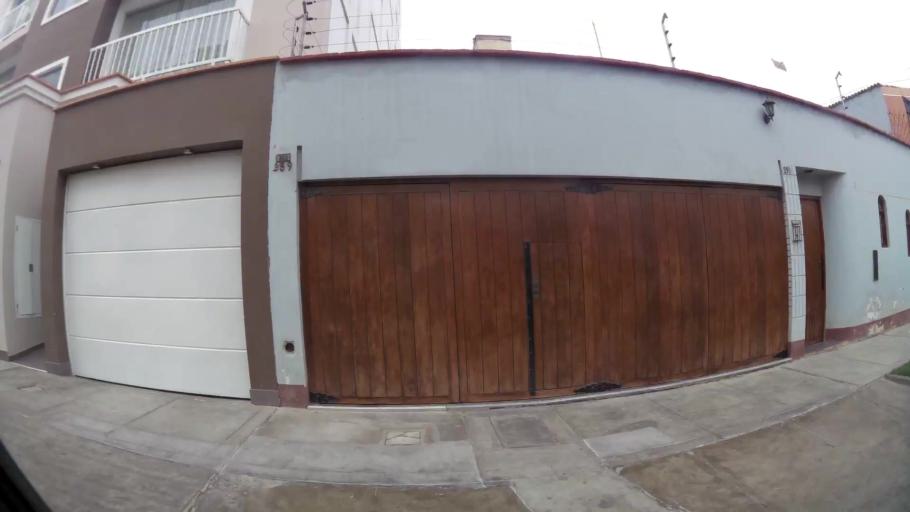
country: PE
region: La Libertad
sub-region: Provincia de Trujillo
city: Buenos Aires
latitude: -8.1344
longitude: -79.0425
